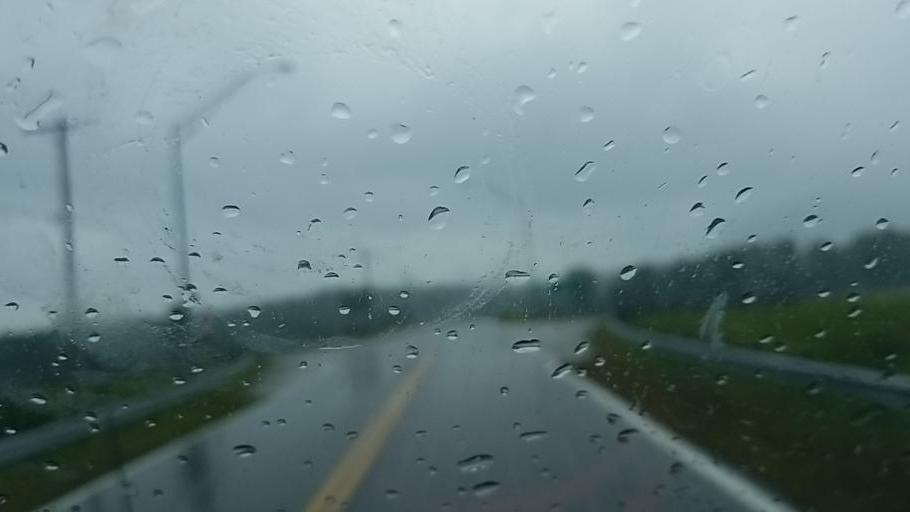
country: US
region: Ohio
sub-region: Logan County
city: Bellefontaine
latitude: 40.3235
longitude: -83.6637
